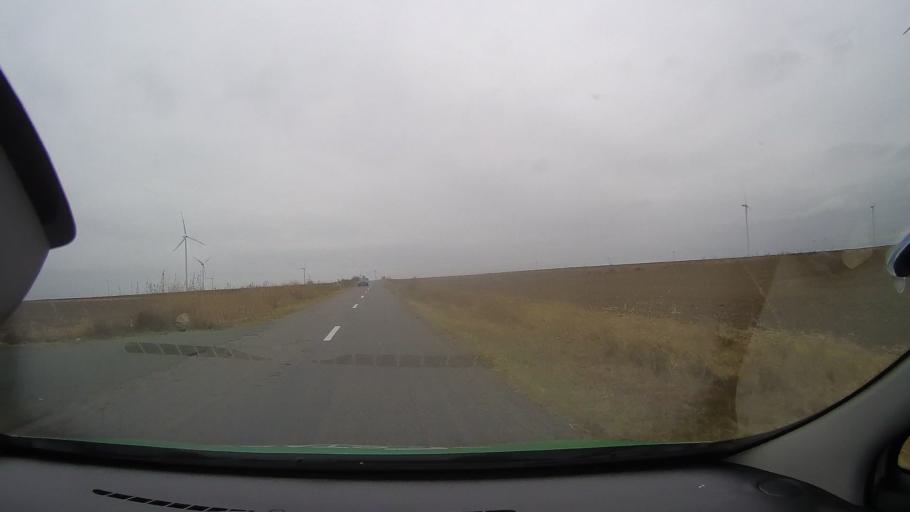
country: RO
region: Constanta
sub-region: Comuna Pantelimon
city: Pantelimon
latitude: 44.5072
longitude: 28.3443
